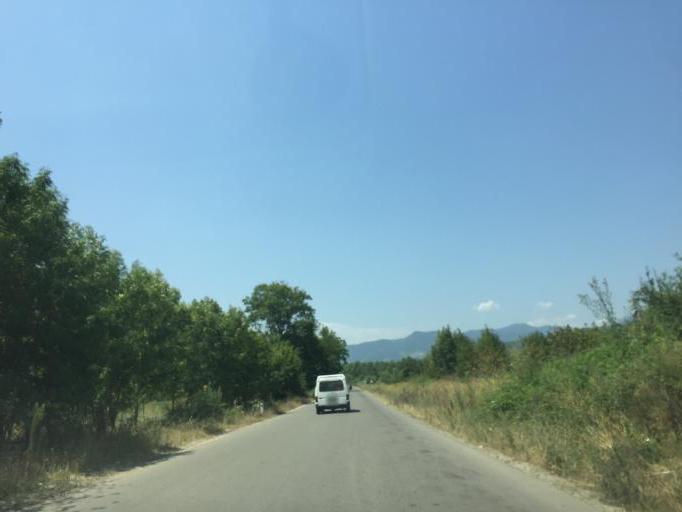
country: AZ
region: Tartar Rayon
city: Martakert
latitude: 40.1401
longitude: 46.5186
